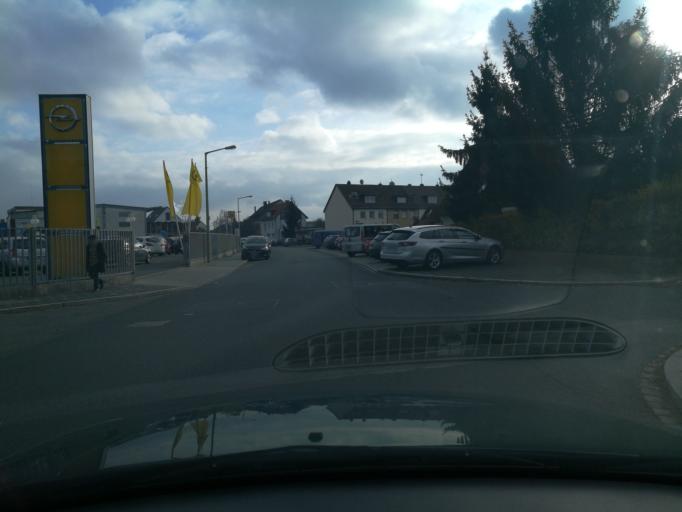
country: DE
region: Bavaria
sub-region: Regierungsbezirk Mittelfranken
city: Grossreuth bei Schweinau
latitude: 49.4533
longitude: 11.0266
